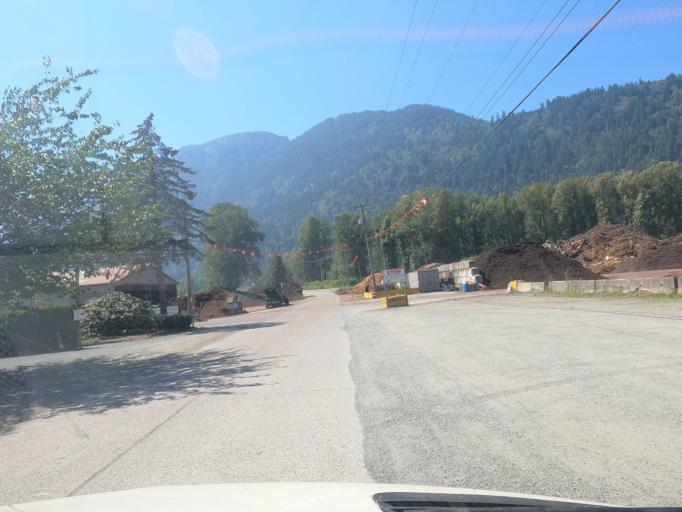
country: CA
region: British Columbia
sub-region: Fraser Valley Regional District
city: Chilliwack
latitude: 49.1257
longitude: -122.0934
